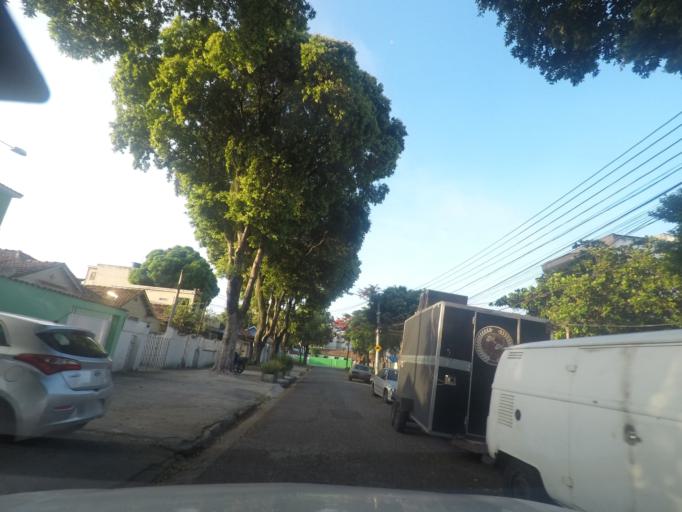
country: BR
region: Rio de Janeiro
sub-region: Duque De Caxias
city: Duque de Caxias
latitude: -22.8326
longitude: -43.2720
